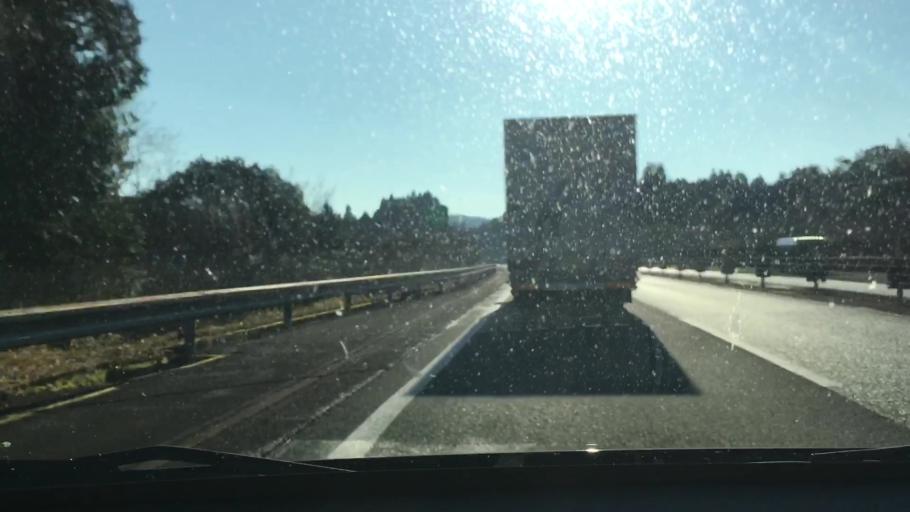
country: JP
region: Kagoshima
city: Kajiki
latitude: 31.8927
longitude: 130.6996
